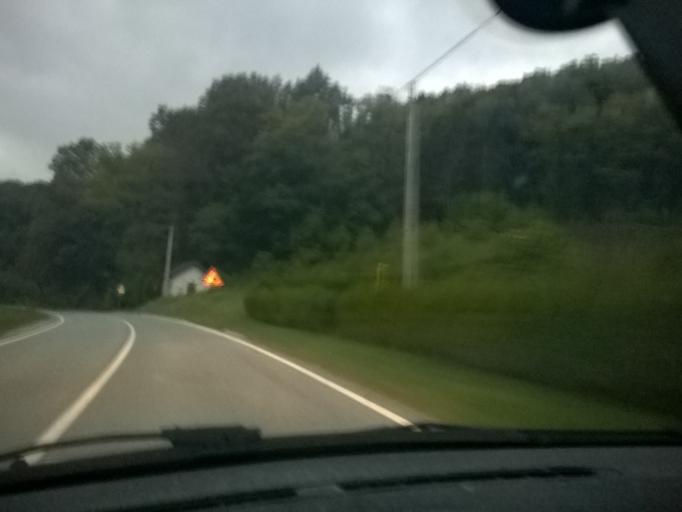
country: SI
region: Zetale
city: Zetale
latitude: 46.2054
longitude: 15.8142
